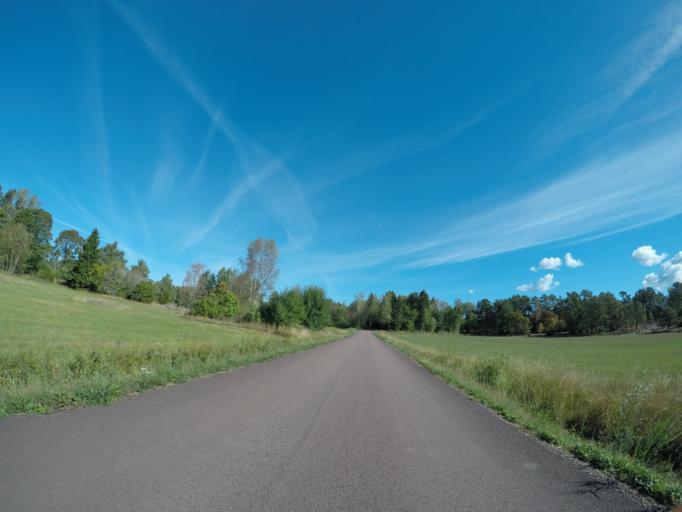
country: AX
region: Alands landsbygd
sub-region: Finstroem
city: Finstroem
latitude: 60.2971
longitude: 19.8796
